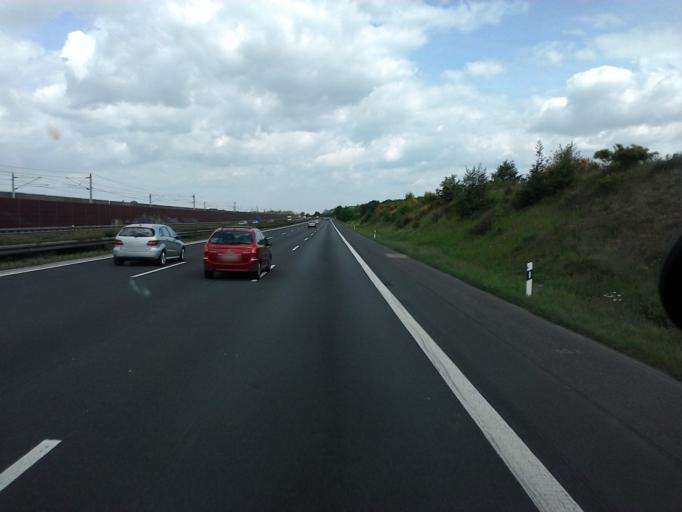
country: DE
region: North Rhine-Westphalia
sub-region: Regierungsbezirk Koln
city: Stossdorf
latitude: 50.7502
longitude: 7.2339
